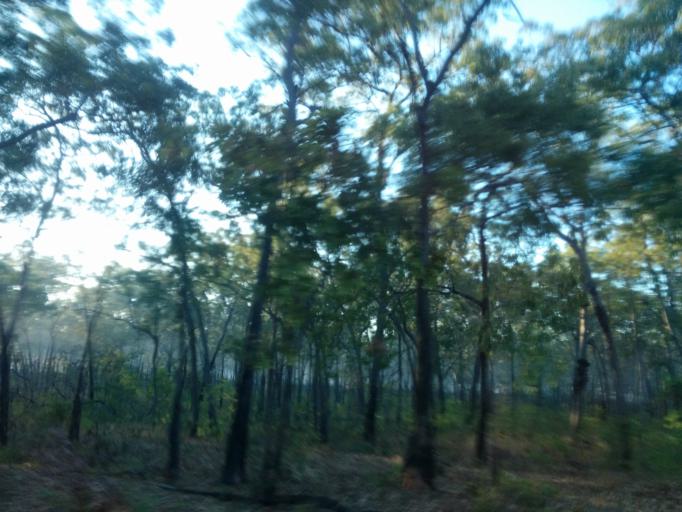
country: AU
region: Northern Territory
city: Alyangula
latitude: -13.8666
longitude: 136.8015
